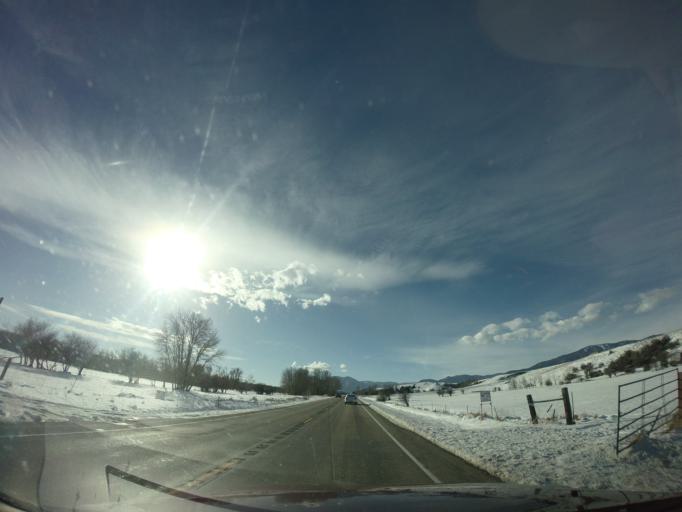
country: US
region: Montana
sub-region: Carbon County
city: Red Lodge
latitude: 45.2425
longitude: -109.2356
